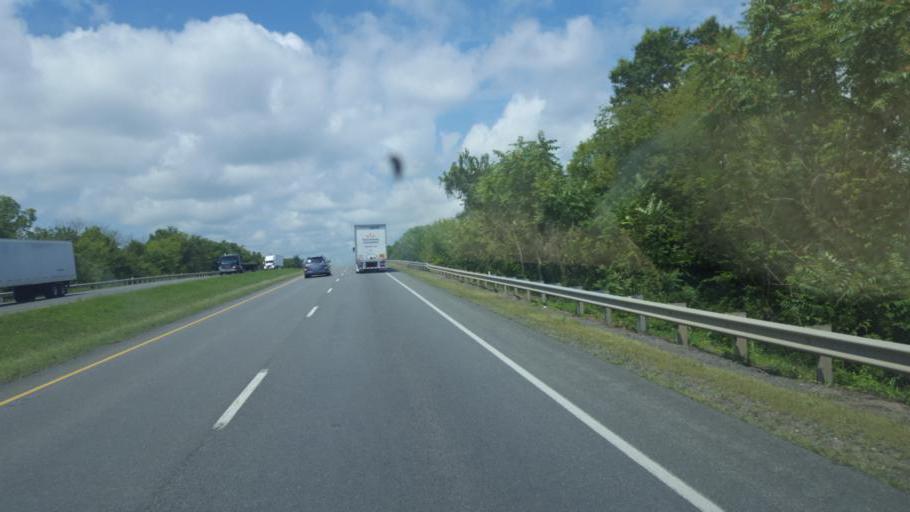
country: US
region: Virginia
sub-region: Fauquier County
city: Bealeton
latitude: 38.5705
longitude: -77.7609
